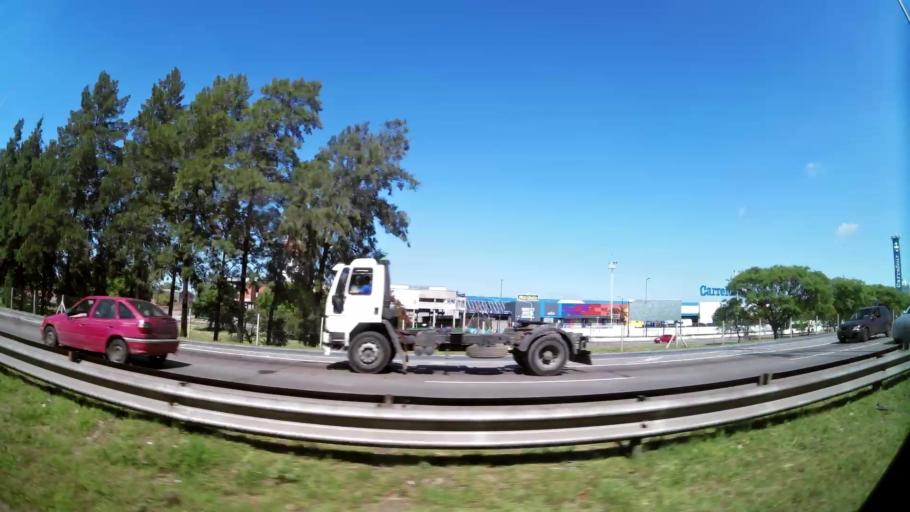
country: AR
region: Buenos Aires
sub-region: Partido de Tigre
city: Tigre
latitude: -34.4546
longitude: -58.5743
